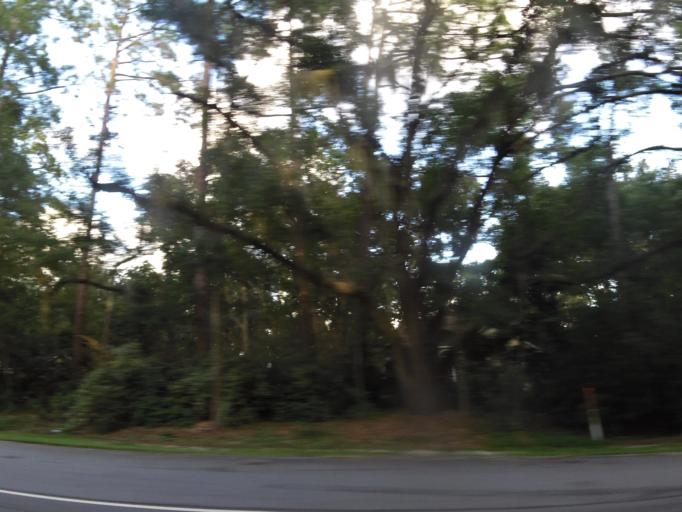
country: US
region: Georgia
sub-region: Glynn County
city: Saint Simon Mills
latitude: 31.1758
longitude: -81.4010
